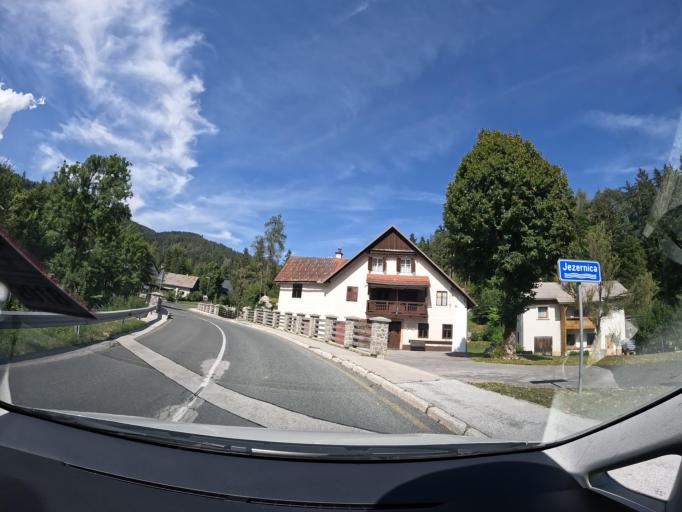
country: AT
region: Carinthia
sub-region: Politischer Bezirk Klagenfurt Land
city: Moosburg
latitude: 46.6573
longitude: 14.1405
